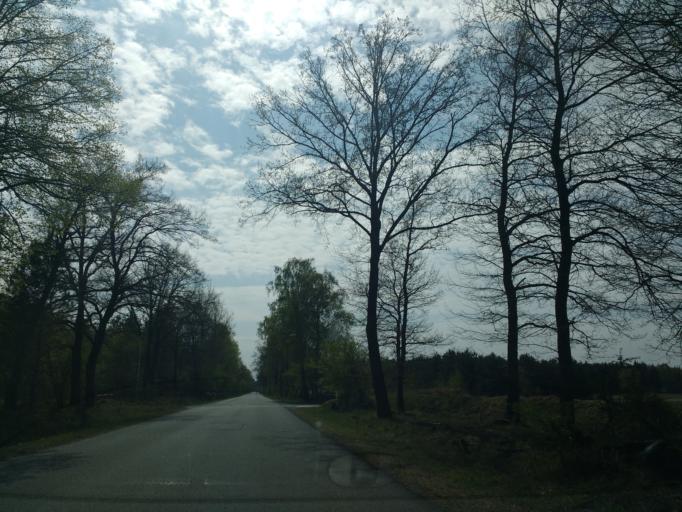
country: DE
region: North Rhine-Westphalia
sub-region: Regierungsbezirk Detmold
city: Hovelhof
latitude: 51.8114
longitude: 8.7224
